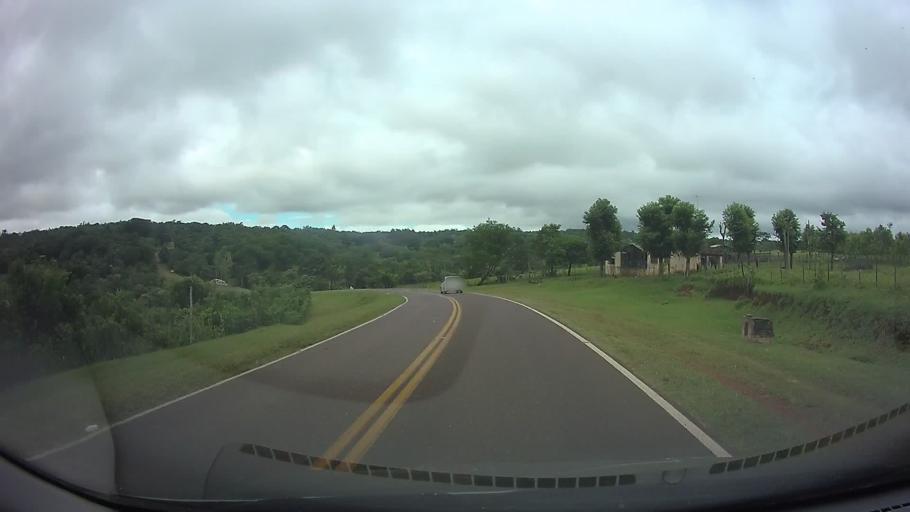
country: PY
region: Paraguari
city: Acahay
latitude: -25.9265
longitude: -57.1079
